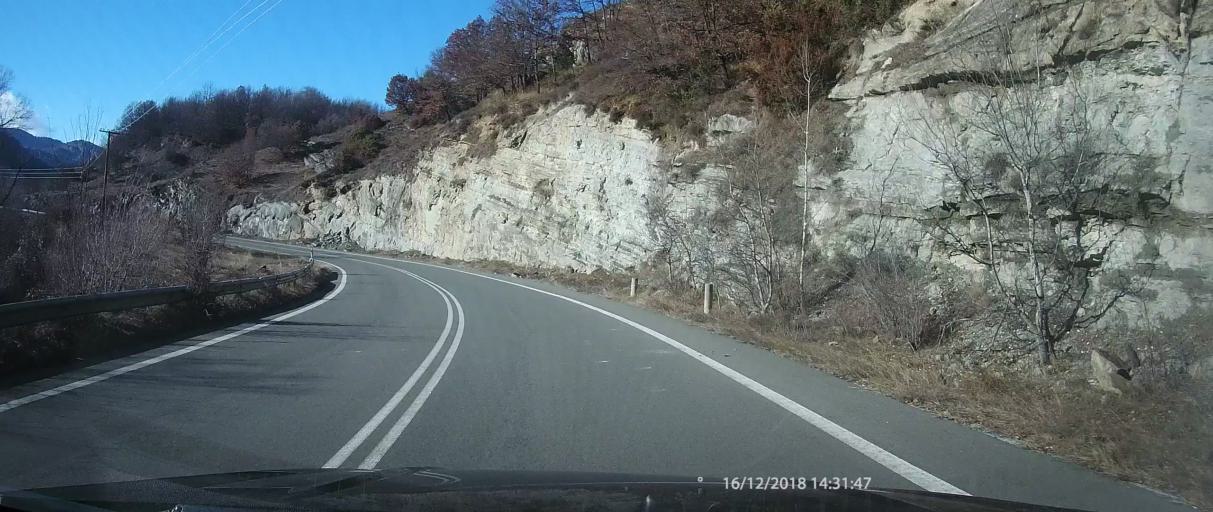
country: GR
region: West Macedonia
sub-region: Nomos Kozanis
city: Tsotili
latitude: 40.1951
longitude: 21.1783
